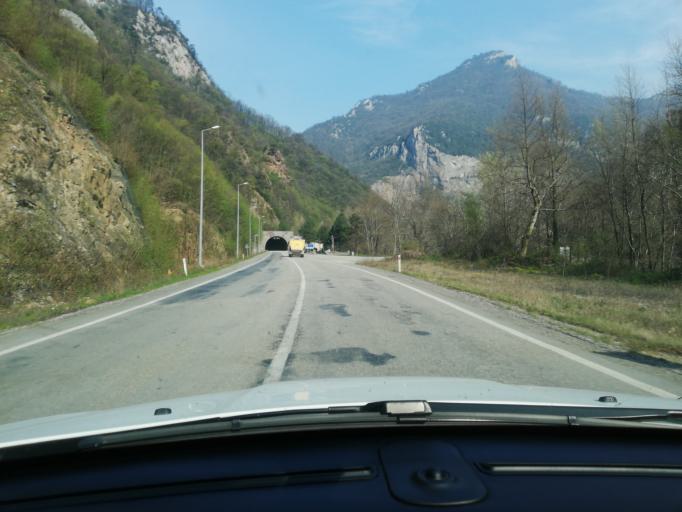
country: TR
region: Karabuk
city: Yenice
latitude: 41.1852
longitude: 32.4456
